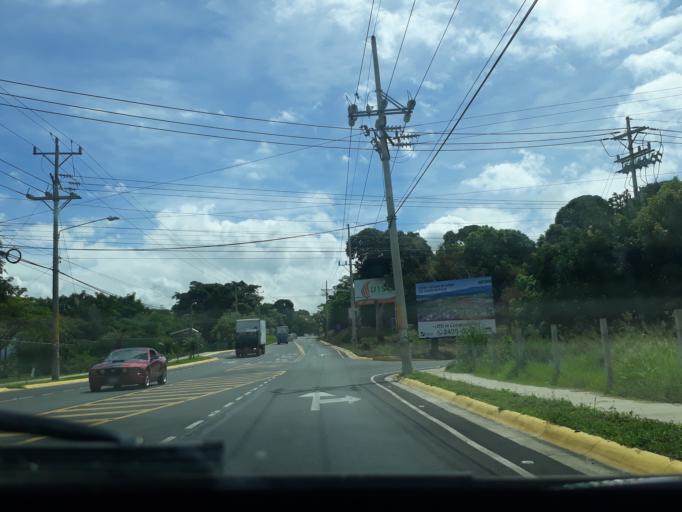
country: CR
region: Alajuela
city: Atenas
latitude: 10.0333
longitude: -84.3540
